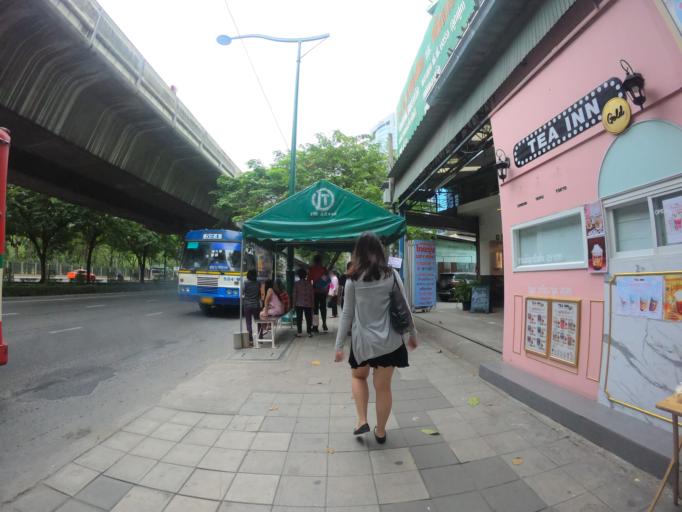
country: TH
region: Bangkok
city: Chatuchak
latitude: 13.8283
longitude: 100.5532
